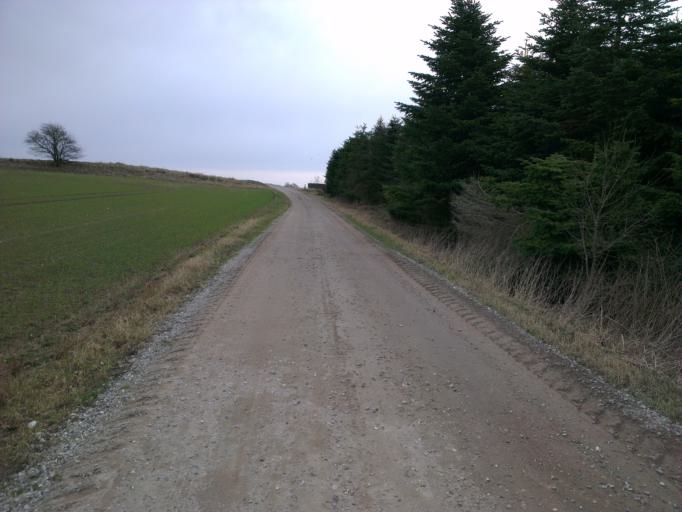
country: DK
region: Zealand
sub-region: Lejre Kommune
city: Ejby
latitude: 55.7662
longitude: 11.8738
